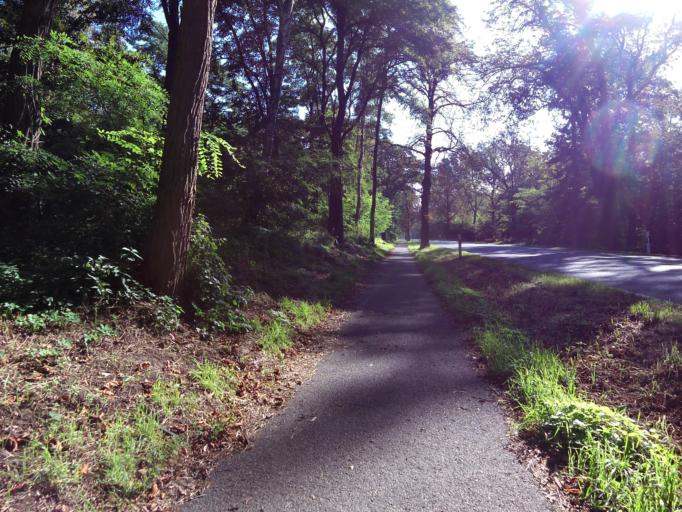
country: DE
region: Saxony-Anhalt
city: Aken
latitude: 51.8496
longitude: 12.1080
